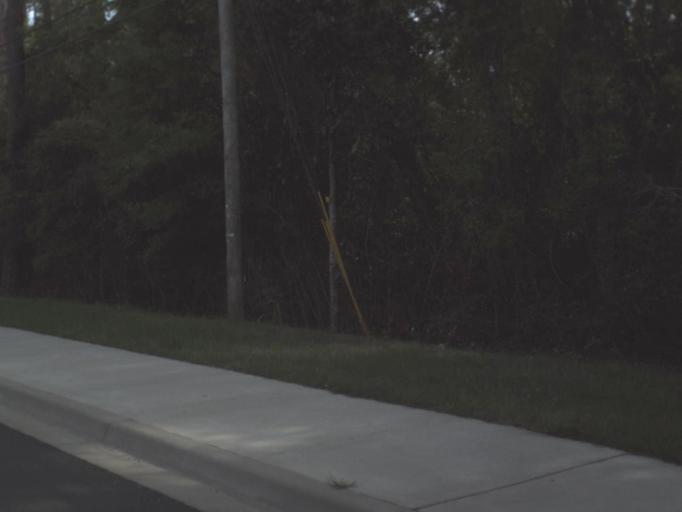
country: US
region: Florida
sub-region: Santa Rosa County
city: Holley
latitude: 30.4520
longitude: -86.9073
